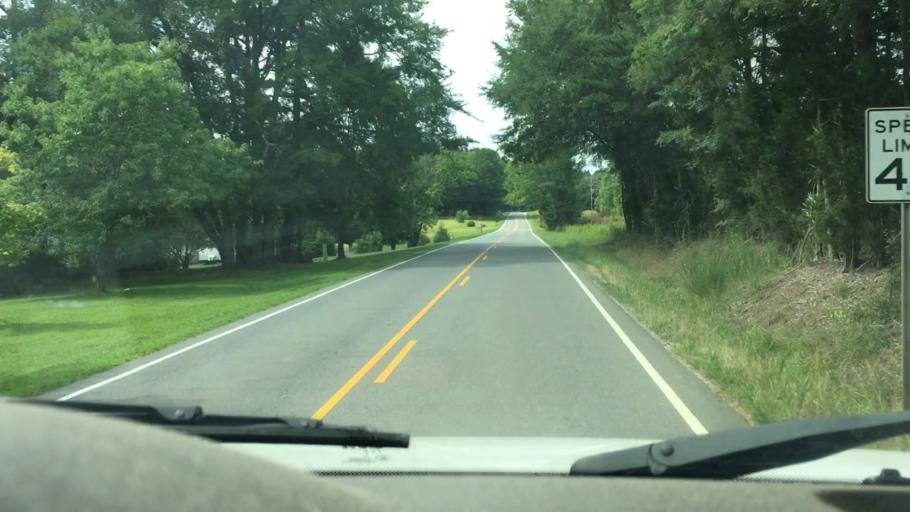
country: US
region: North Carolina
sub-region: Gaston County
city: Davidson
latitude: 35.4771
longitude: -80.8029
